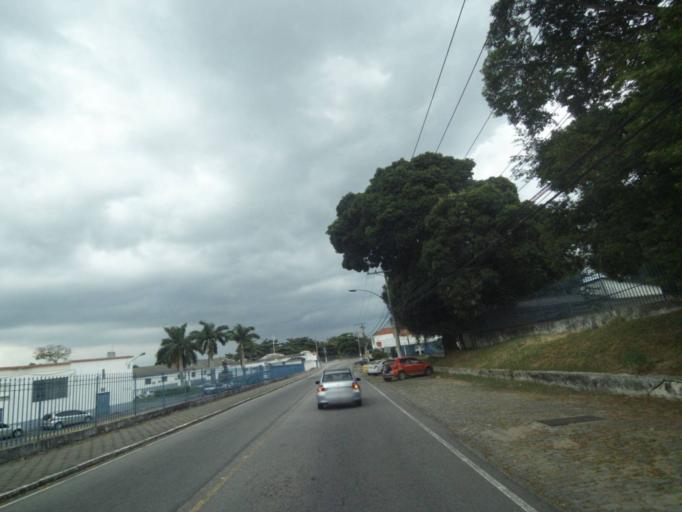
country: BR
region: Rio de Janeiro
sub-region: Sao Joao De Meriti
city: Sao Joao de Meriti
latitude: -22.8804
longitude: -43.3814
